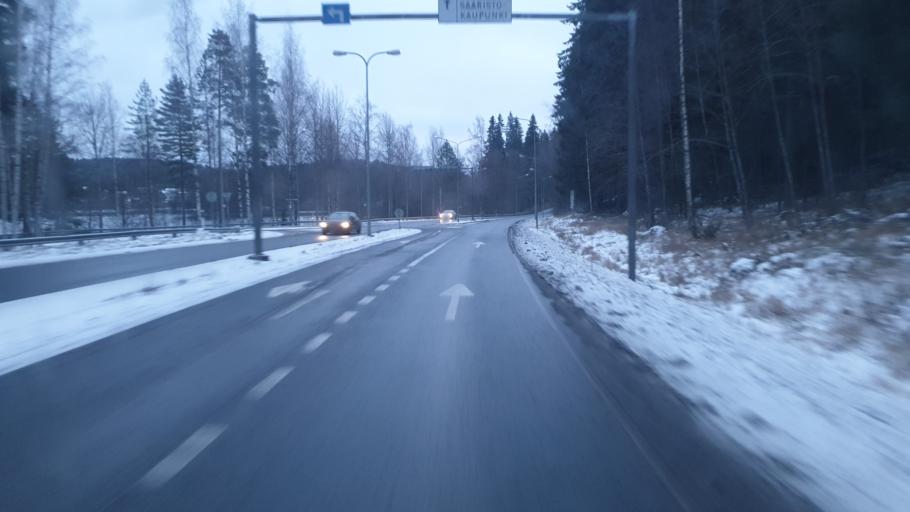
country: FI
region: Northern Savo
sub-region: Kuopio
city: Kuopio
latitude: 62.8446
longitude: 27.6264
